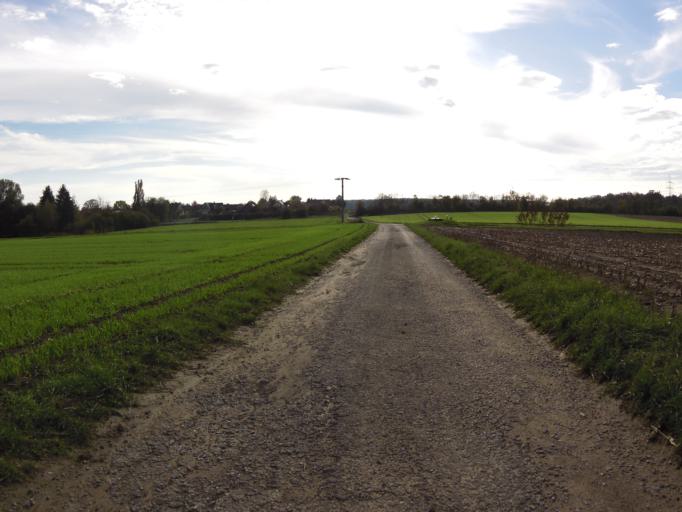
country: DE
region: Bavaria
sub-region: Regierungsbezirk Unterfranken
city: Frickenhausen
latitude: 49.7101
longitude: 10.0756
